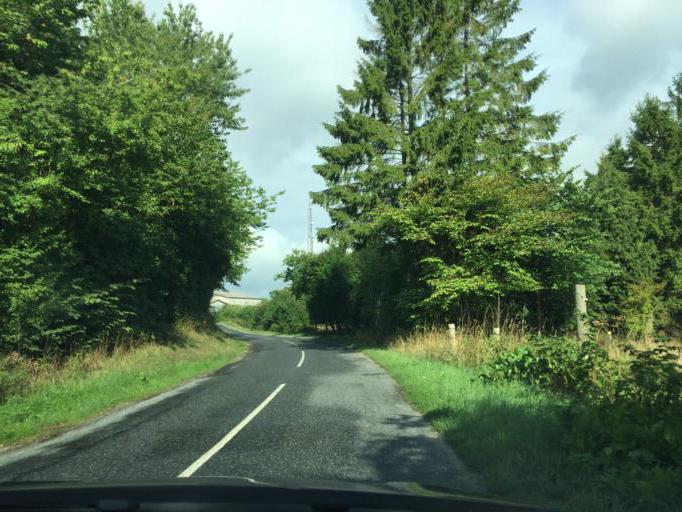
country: DK
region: South Denmark
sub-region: Assens Kommune
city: Harby
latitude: 55.2023
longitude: 10.1712
